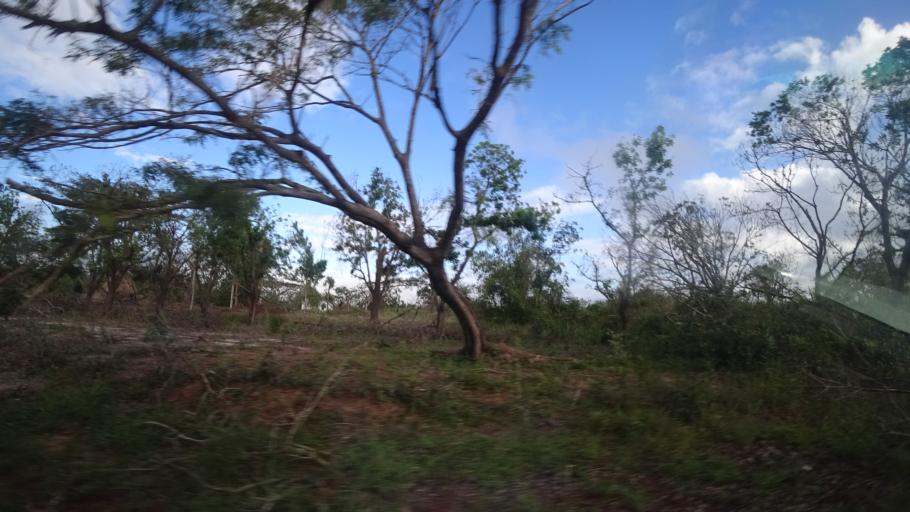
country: MZ
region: Sofala
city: Beira
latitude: -19.6482
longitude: 35.0586
